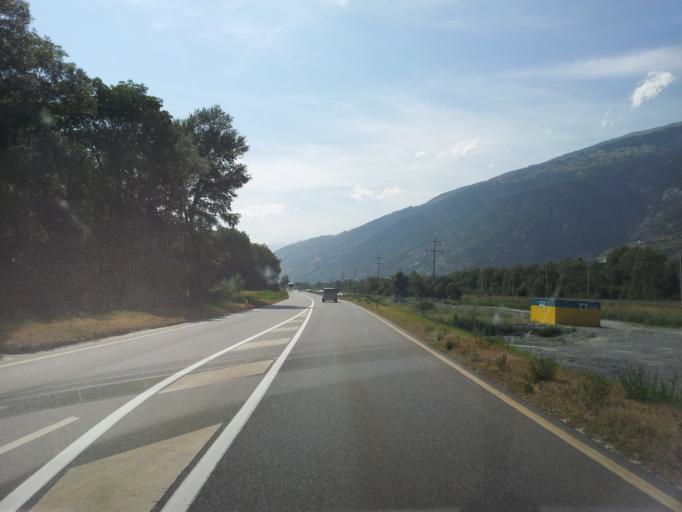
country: CH
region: Valais
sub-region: Raron District
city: Raron
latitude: 46.3063
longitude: 7.7717
